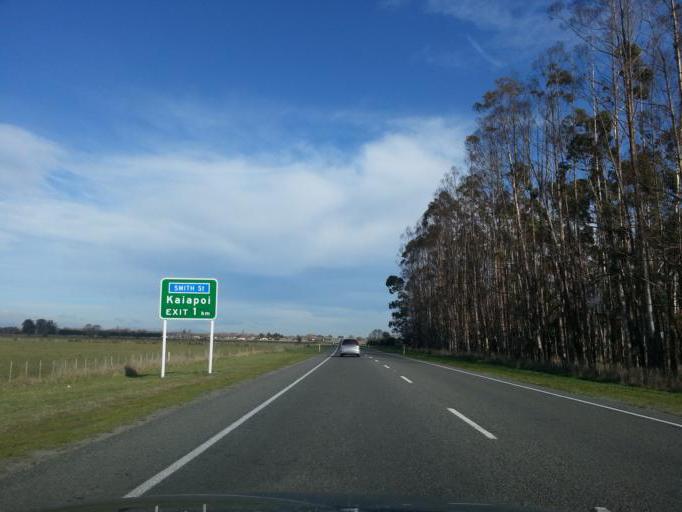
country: NZ
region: Canterbury
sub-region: Waimakariri District
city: Kaiapoi
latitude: -43.3635
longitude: 172.6517
